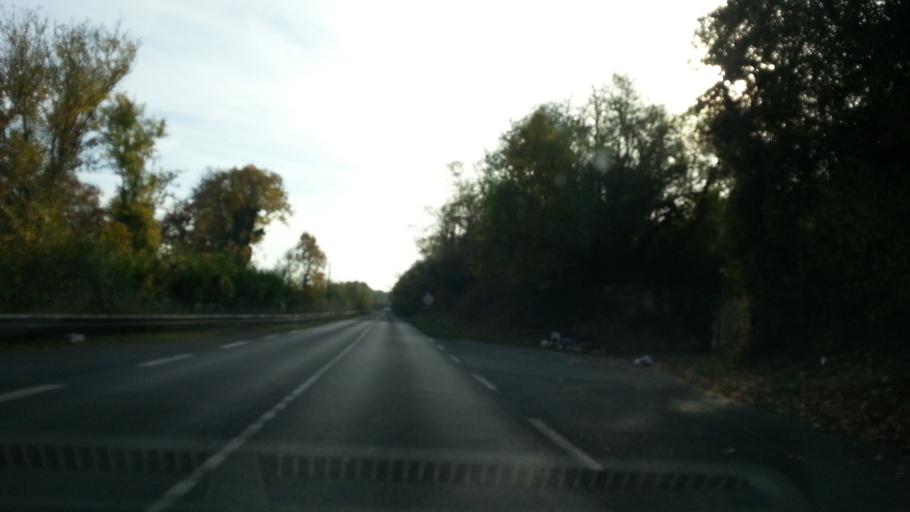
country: FR
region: Picardie
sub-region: Departement de l'Oise
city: Precy-sur-Oise
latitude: 49.1910
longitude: 2.3644
